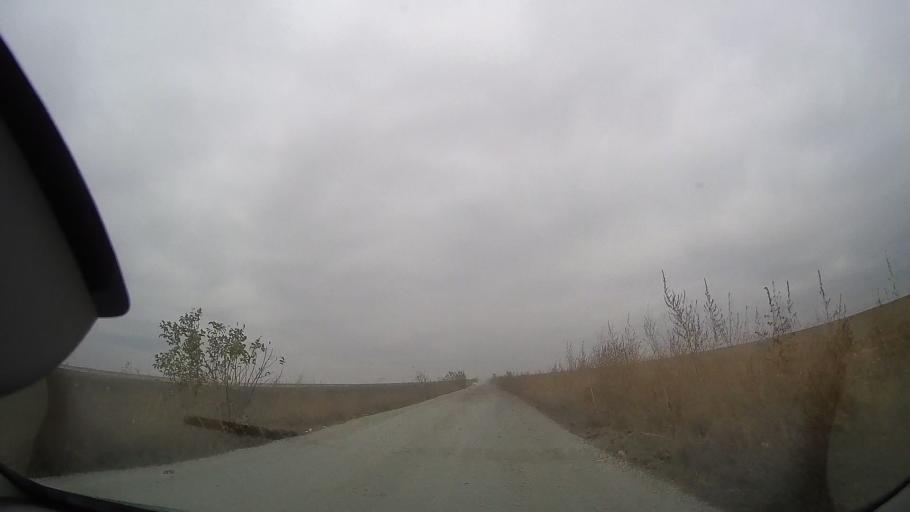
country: RO
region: Ialomita
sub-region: Comuna Grivita
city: Grivita
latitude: 44.7465
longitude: 27.2682
